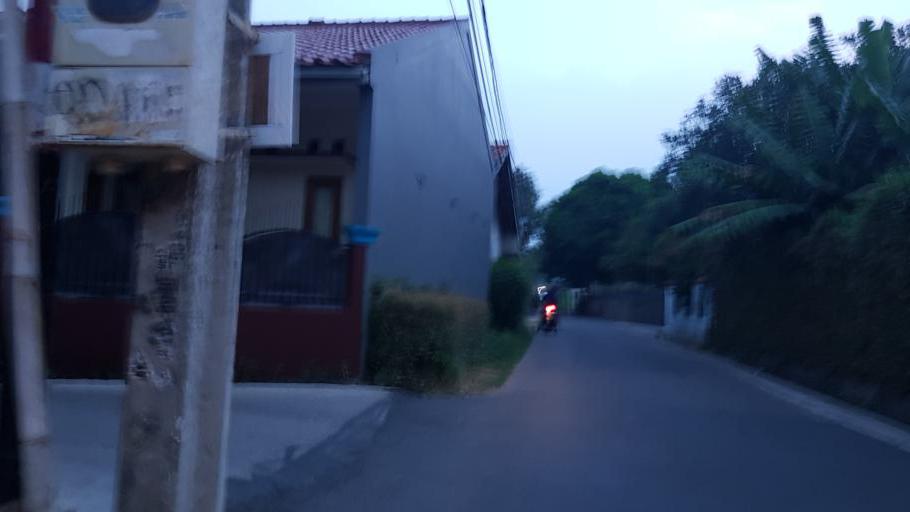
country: ID
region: West Java
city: Pamulang
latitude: -6.3326
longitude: 106.7945
